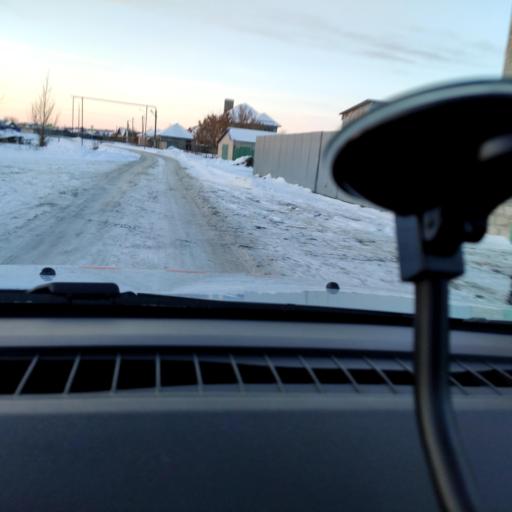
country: RU
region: Samara
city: Dubovyy Umet
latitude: 53.0797
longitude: 50.2252
